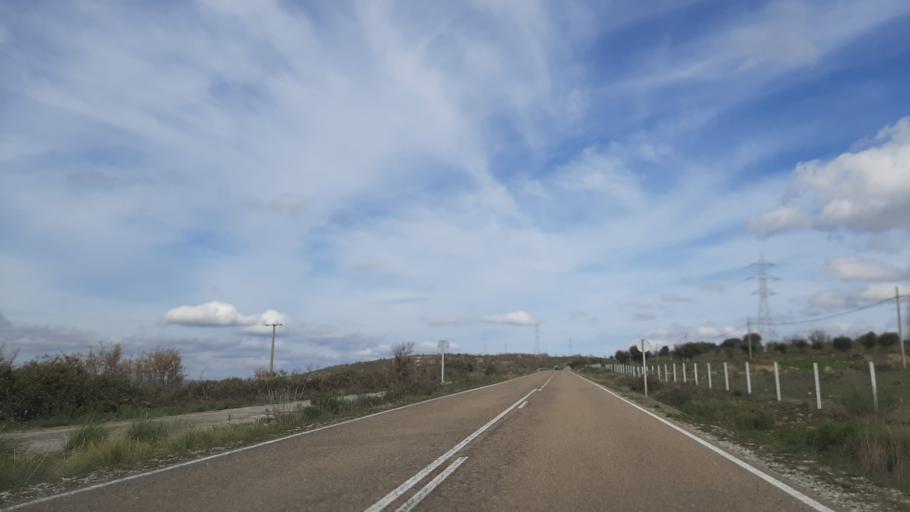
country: ES
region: Castille and Leon
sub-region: Provincia de Salamanca
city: Villarino de los Aires
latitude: 41.2389
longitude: -6.5145
